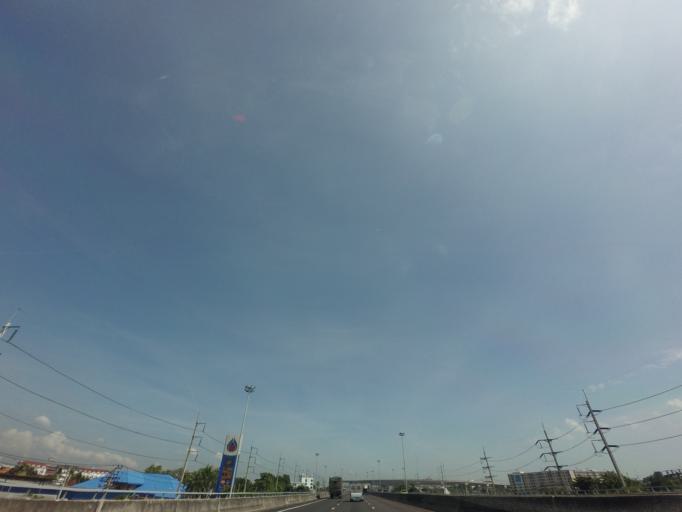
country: TH
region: Bangkok
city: Bang Khen
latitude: 13.8444
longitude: 100.6369
